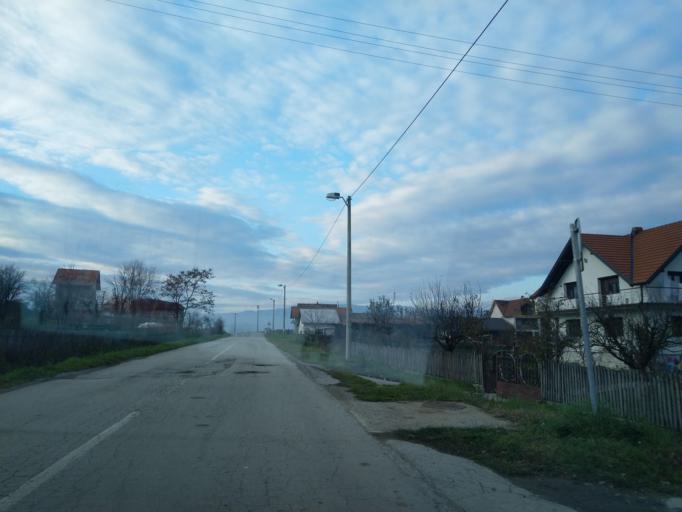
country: RS
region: Central Serbia
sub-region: Zlatiborski Okrug
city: Kosjeric
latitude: 43.9202
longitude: 19.9057
